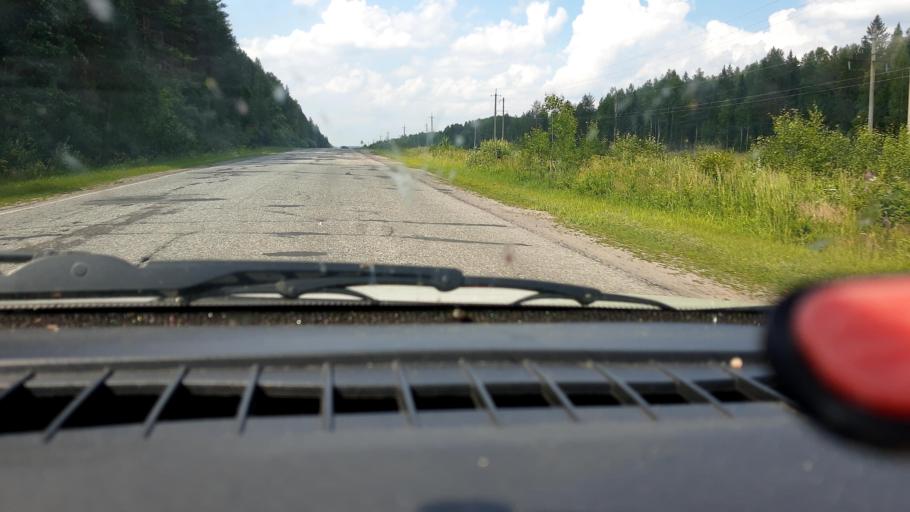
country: RU
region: Nizjnij Novgorod
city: Prudy
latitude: 57.4141
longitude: 46.0710
